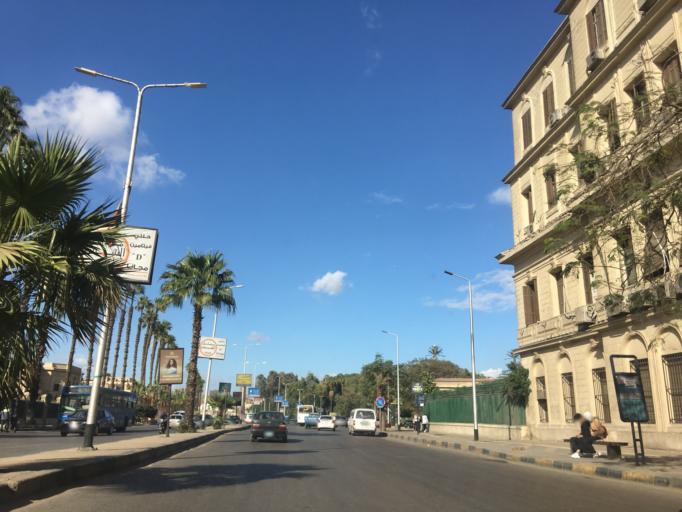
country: EG
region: Al Jizah
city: Al Jizah
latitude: 30.0257
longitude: 31.2109
